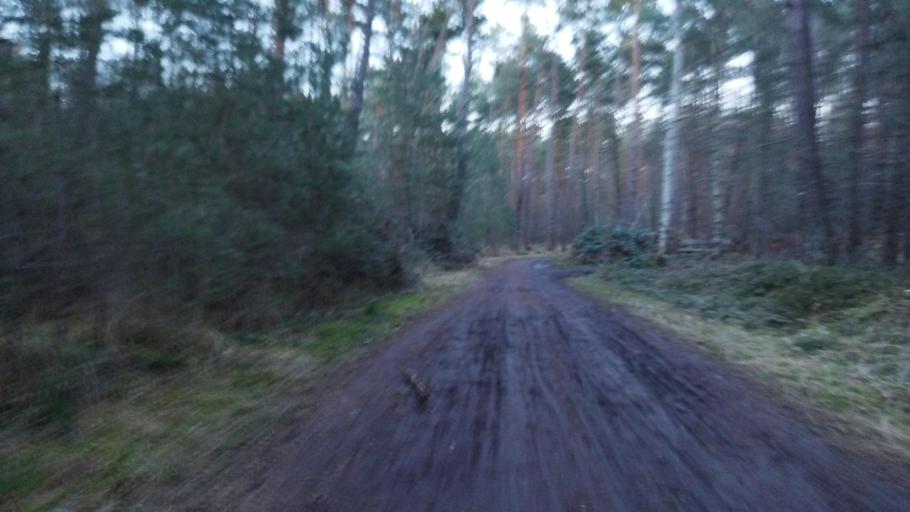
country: DE
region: Rheinland-Pfalz
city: Hanhofen
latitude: 49.3261
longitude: 8.3538
